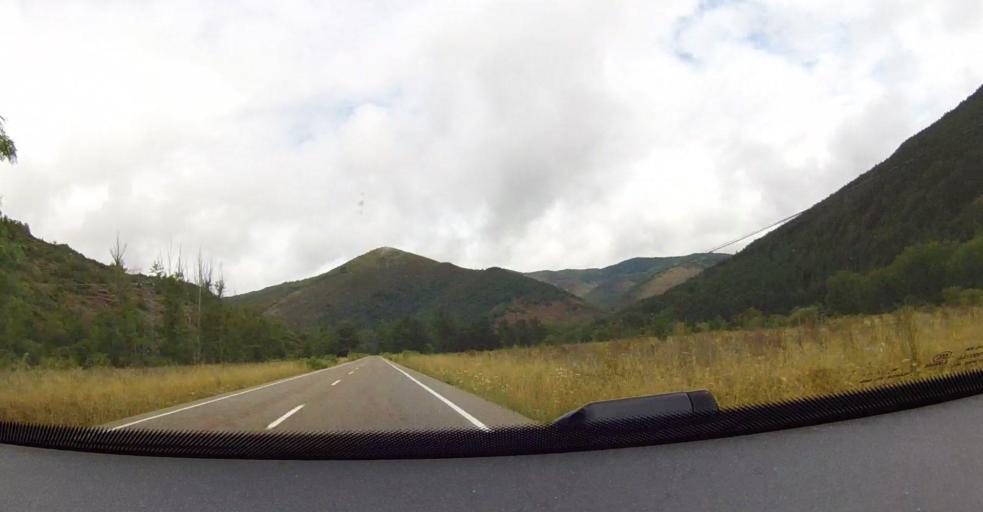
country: ES
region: Castille and Leon
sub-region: Provincia de Leon
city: Bonar
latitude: 42.8818
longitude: -5.3139
